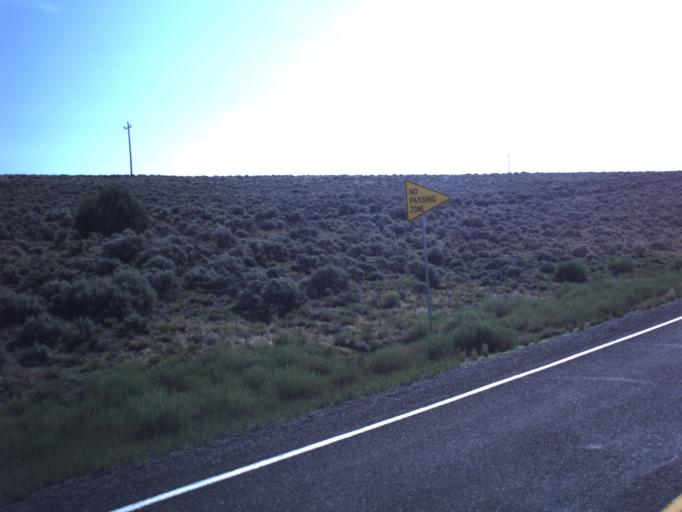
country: US
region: Utah
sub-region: Wayne County
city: Loa
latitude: 38.4408
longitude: -111.7835
